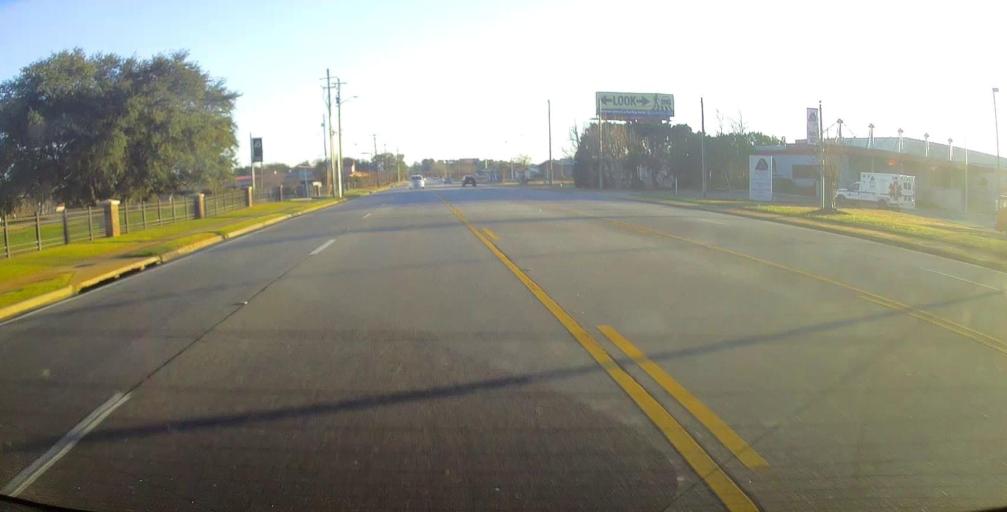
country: US
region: Georgia
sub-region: Dougherty County
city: Albany
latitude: 31.5552
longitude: -84.1766
